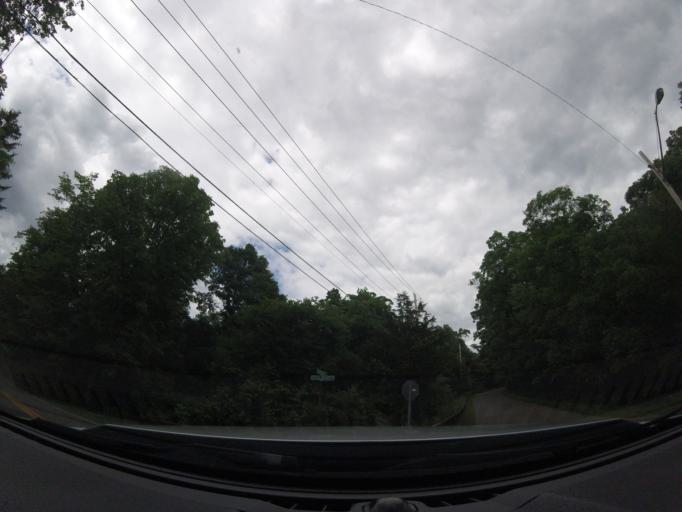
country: US
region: New York
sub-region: Tompkins County
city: Cayuga Heights
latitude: 42.4729
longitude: -76.4969
